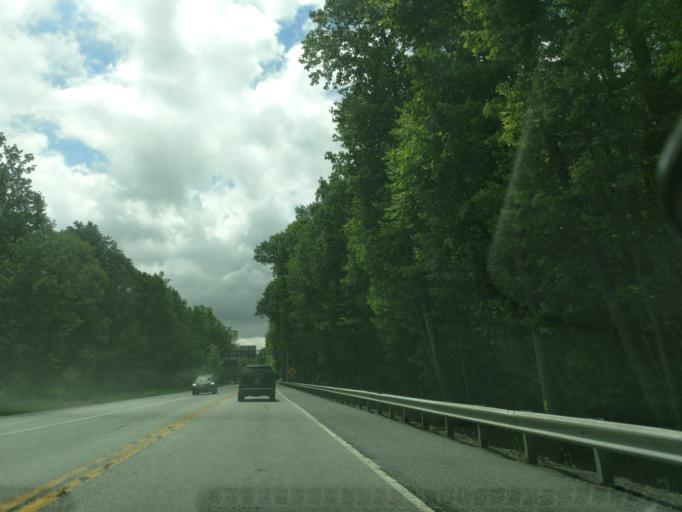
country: US
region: Pennsylvania
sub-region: Lebanon County
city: Cornwall
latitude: 40.2547
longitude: -76.4318
